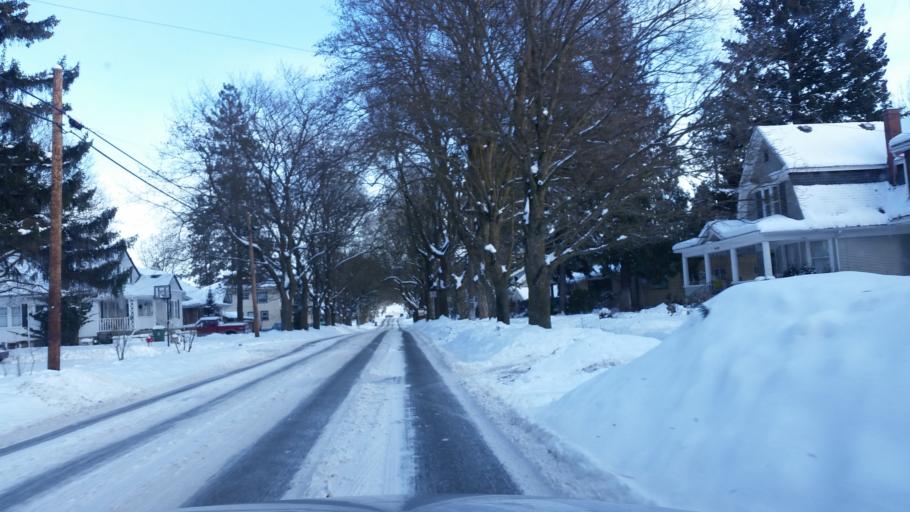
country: US
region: Washington
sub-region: Spokane County
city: Spokane
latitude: 47.6427
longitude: -117.4135
